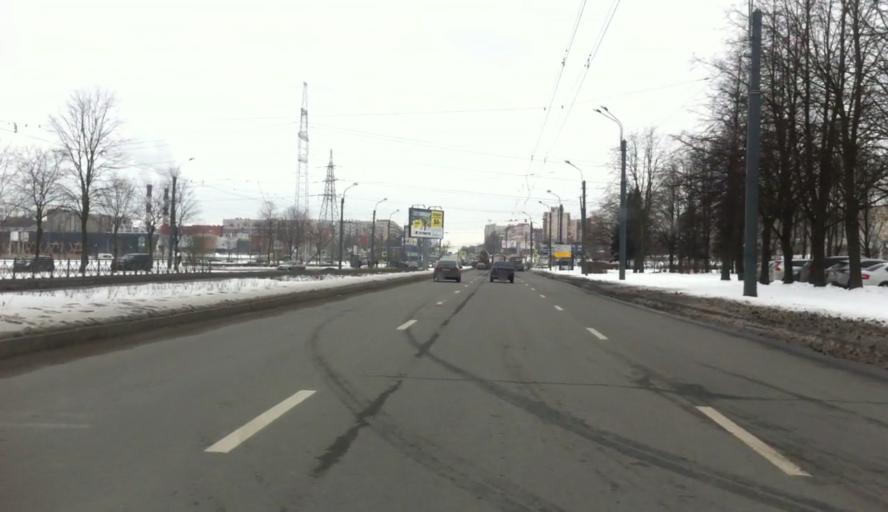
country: RU
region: St.-Petersburg
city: Uritsk
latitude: 59.8493
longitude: 30.1754
